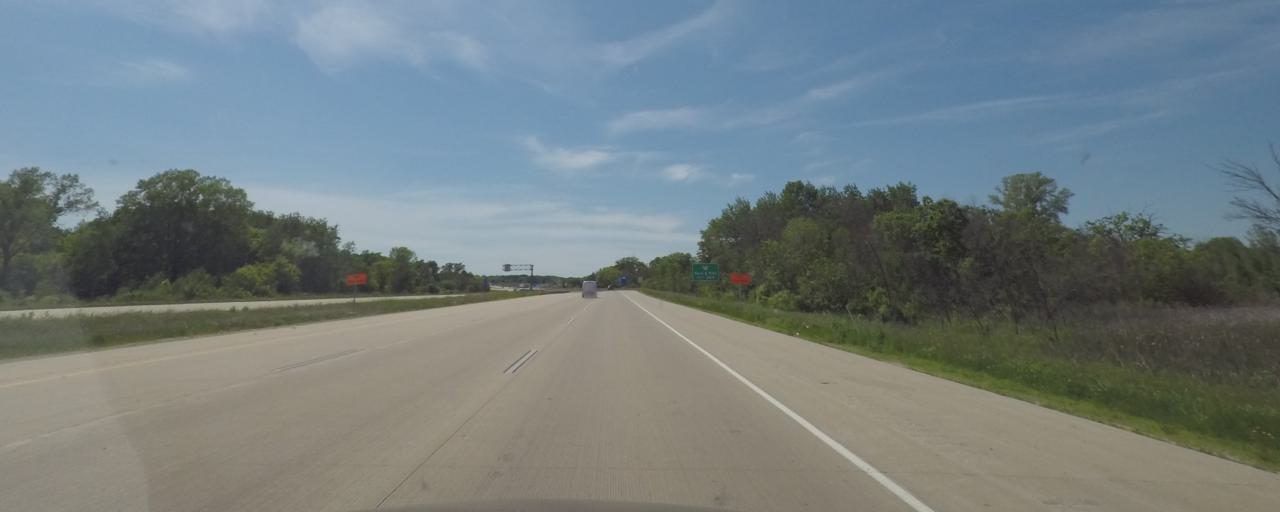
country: US
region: Wisconsin
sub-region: Dane County
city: Cottage Grove
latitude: 43.1100
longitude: -89.1824
